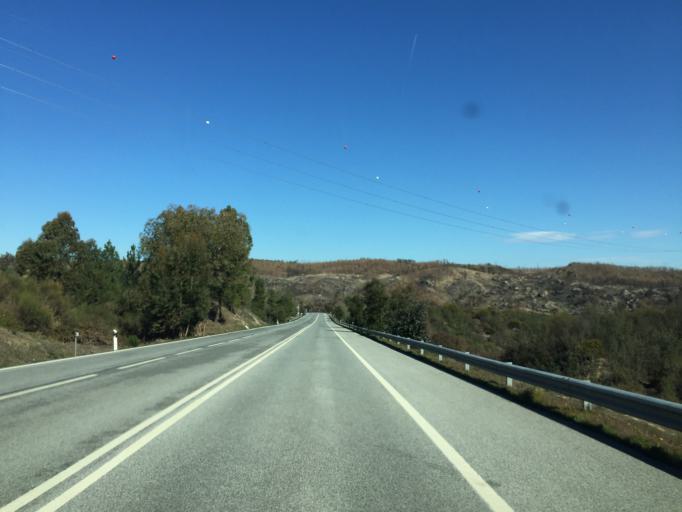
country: PT
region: Portalegre
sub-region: Nisa
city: Nisa
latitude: 39.5095
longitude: -7.7703
